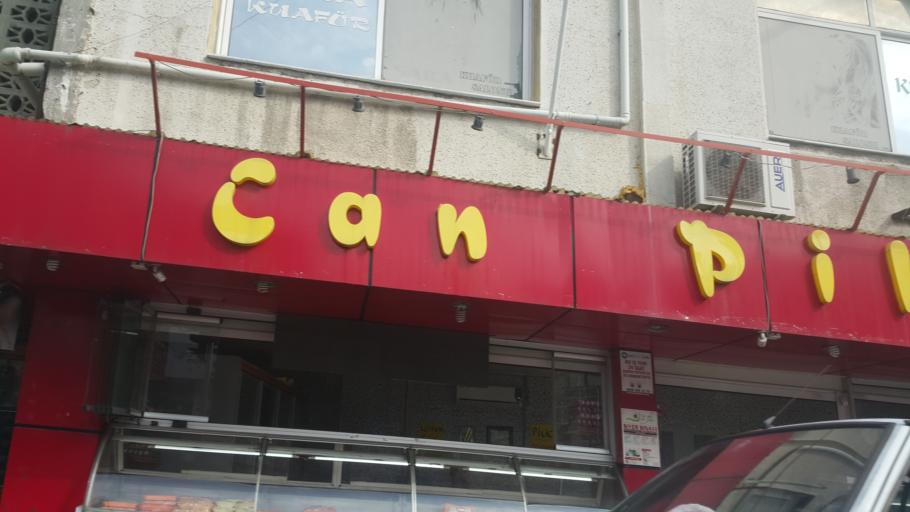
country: TR
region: Mersin
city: Tarsus
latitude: 36.9153
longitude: 34.8939
